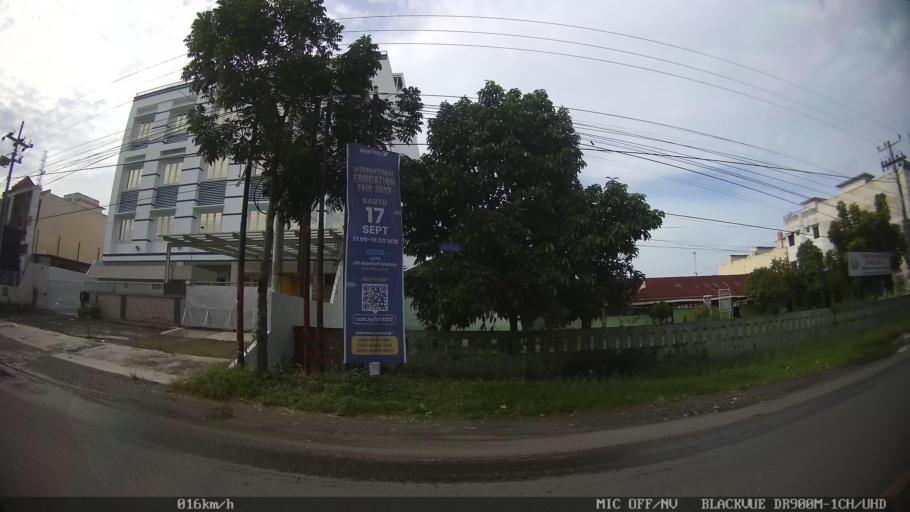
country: ID
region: North Sumatra
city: Medan
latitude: 3.6287
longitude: 98.6994
